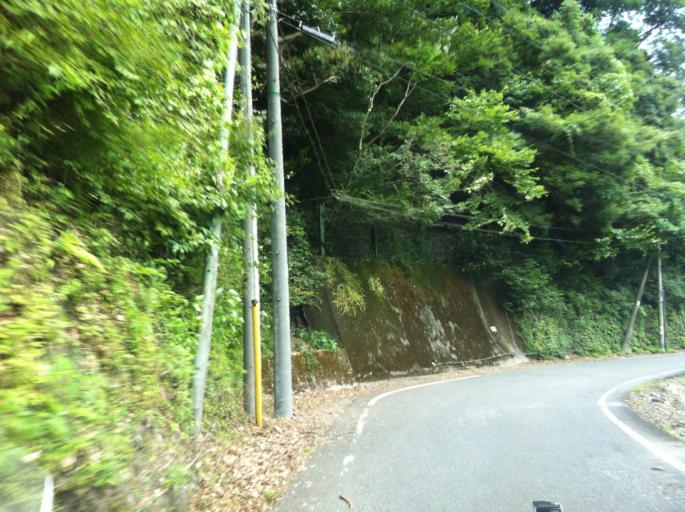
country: JP
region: Shizuoka
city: Shizuoka-shi
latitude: 35.2072
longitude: 138.3538
